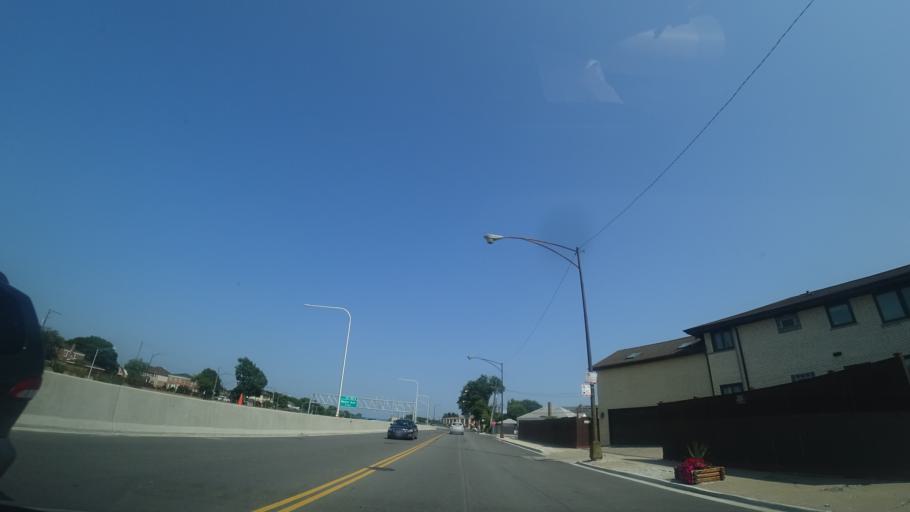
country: US
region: Illinois
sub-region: Cook County
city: Harwood Heights
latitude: 41.9823
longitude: -87.8149
